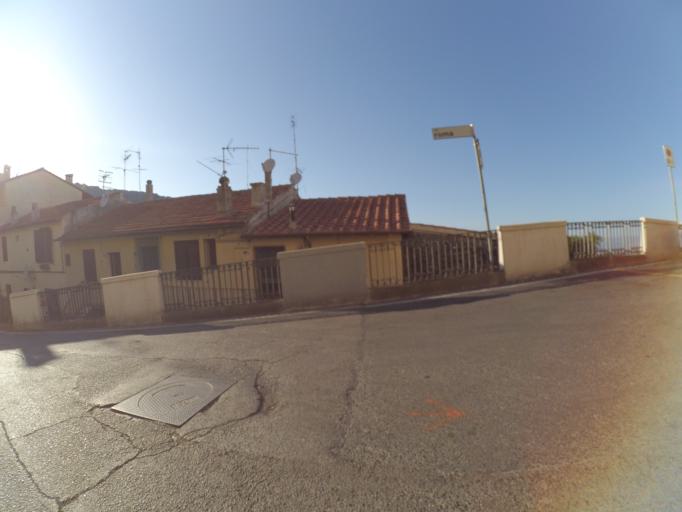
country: IT
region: Latium
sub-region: Provincia di Latina
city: San Felice Circeo
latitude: 41.2335
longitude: 13.0884
